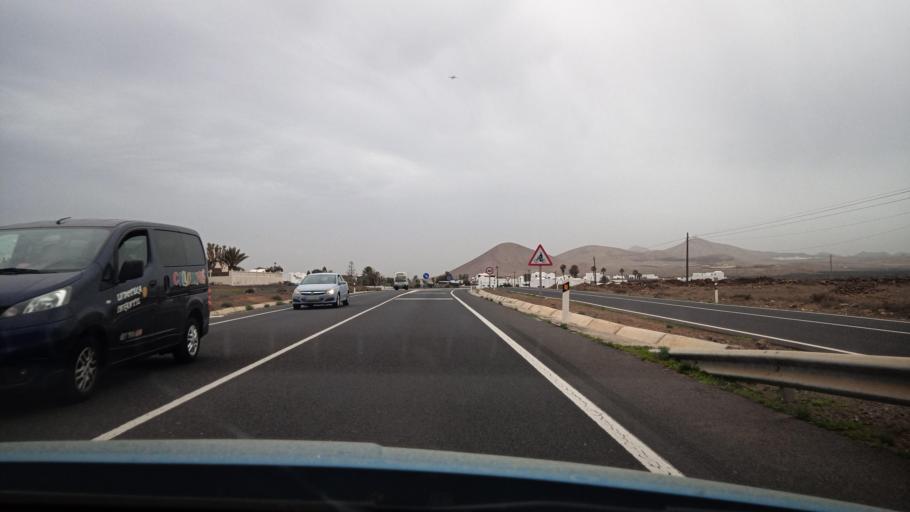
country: ES
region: Canary Islands
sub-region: Provincia de Las Palmas
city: Nazaret
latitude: 29.0200
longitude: -13.5380
